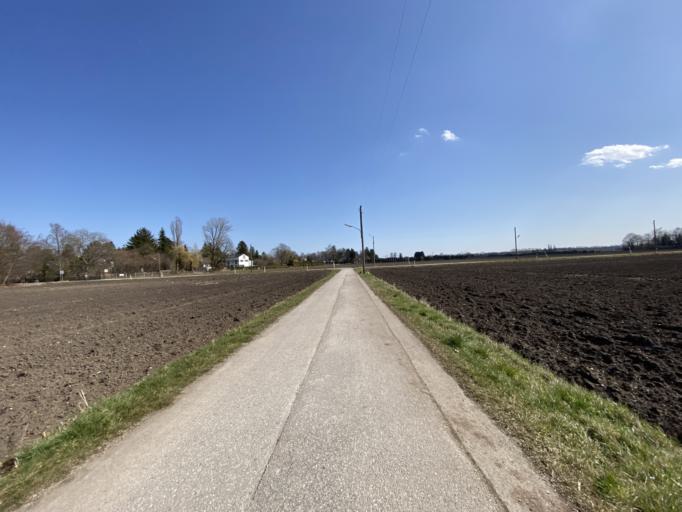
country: DE
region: Bavaria
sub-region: Upper Bavaria
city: Unterfoehring
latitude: 48.1631
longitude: 11.6560
